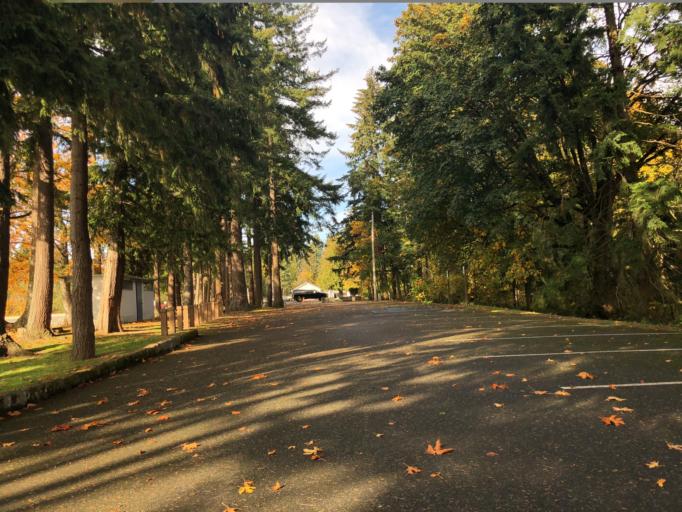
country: US
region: Washington
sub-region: Pierce County
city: Bonney Lake
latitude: 47.2398
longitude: -122.1656
